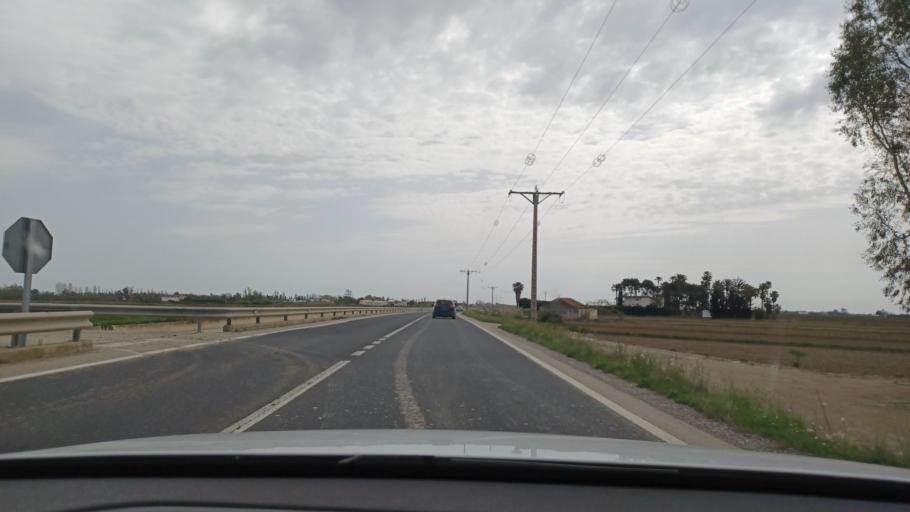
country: ES
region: Catalonia
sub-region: Provincia de Tarragona
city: Deltebre
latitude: 40.7112
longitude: 0.6733
